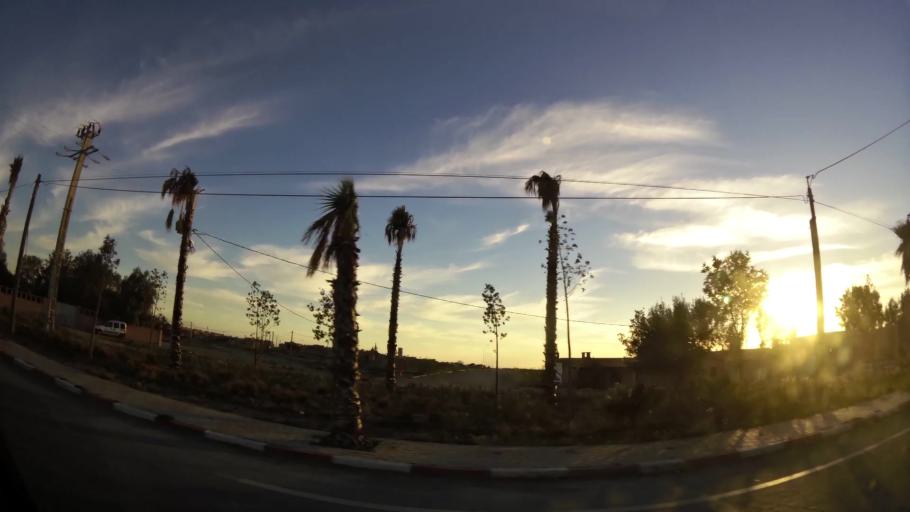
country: MA
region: Marrakech-Tensift-Al Haouz
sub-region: Marrakech
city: Marrakesh
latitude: 31.7602
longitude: -8.1150
